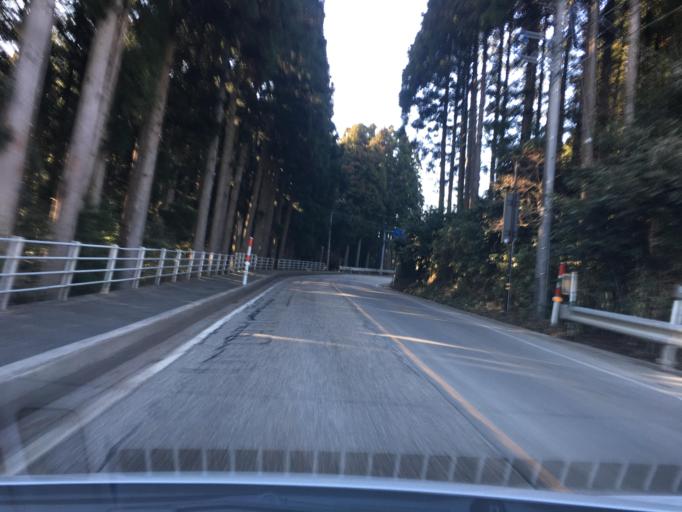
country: JP
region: Ishikawa
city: Nanao
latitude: 36.9803
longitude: 137.0501
